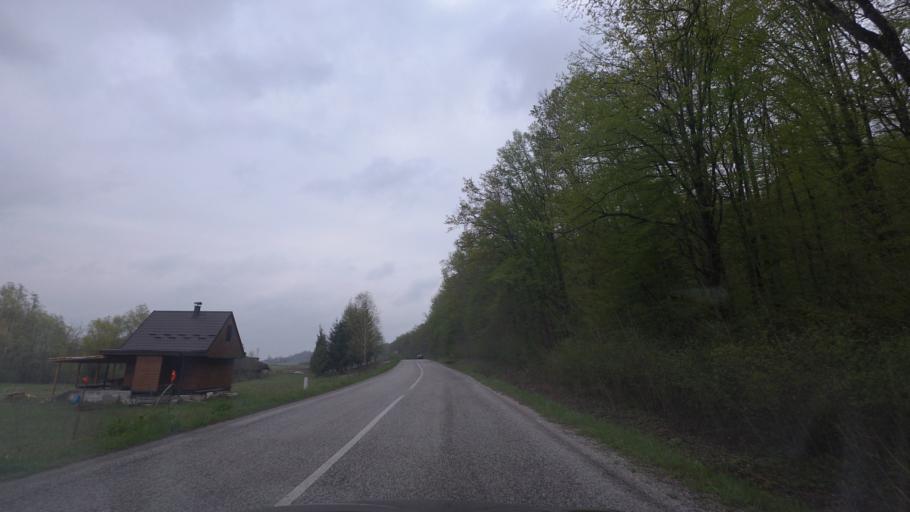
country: HR
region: Karlovacka
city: Ozalj
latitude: 45.6277
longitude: 15.5521
